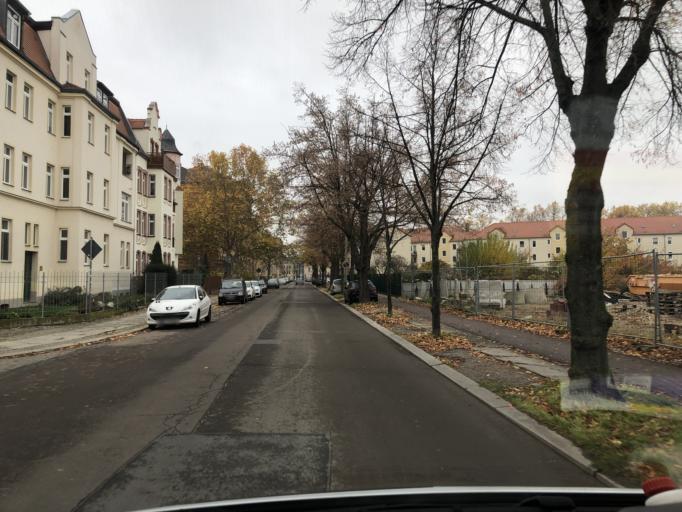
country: DE
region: Saxony-Anhalt
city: Halle (Saale)
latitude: 51.4690
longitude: 11.9751
